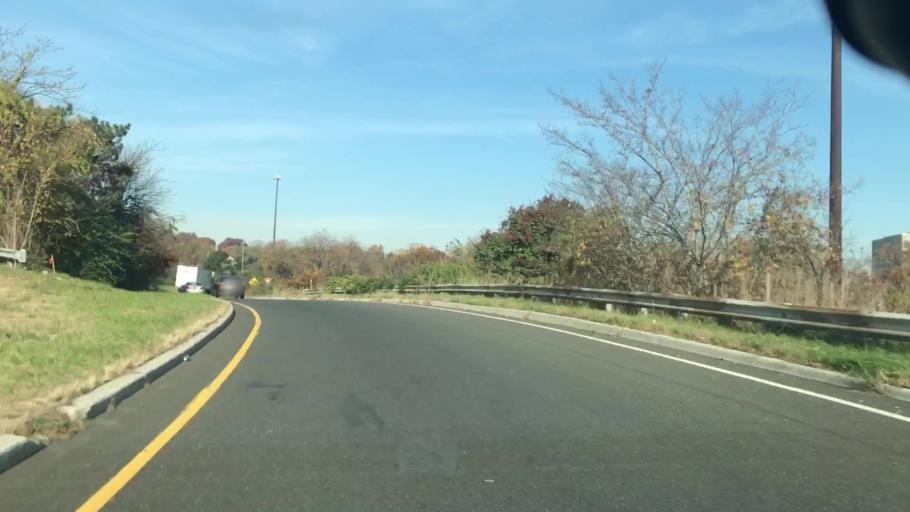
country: US
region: New Jersey
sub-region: Bergen County
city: Rutherford
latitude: 40.8121
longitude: -74.1004
